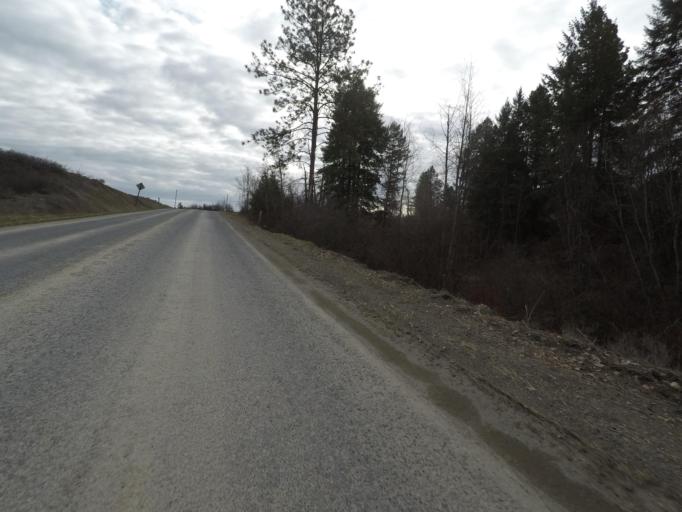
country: US
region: Washington
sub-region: Stevens County
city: Colville
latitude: 48.5185
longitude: -117.8758
